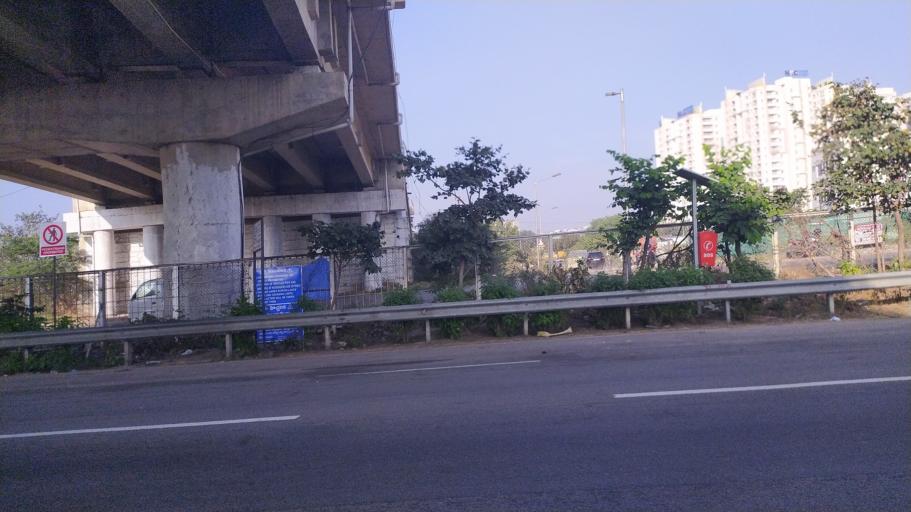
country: IN
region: Telangana
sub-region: Hyderabad
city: Hyderabad
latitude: 17.3862
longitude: 78.3511
